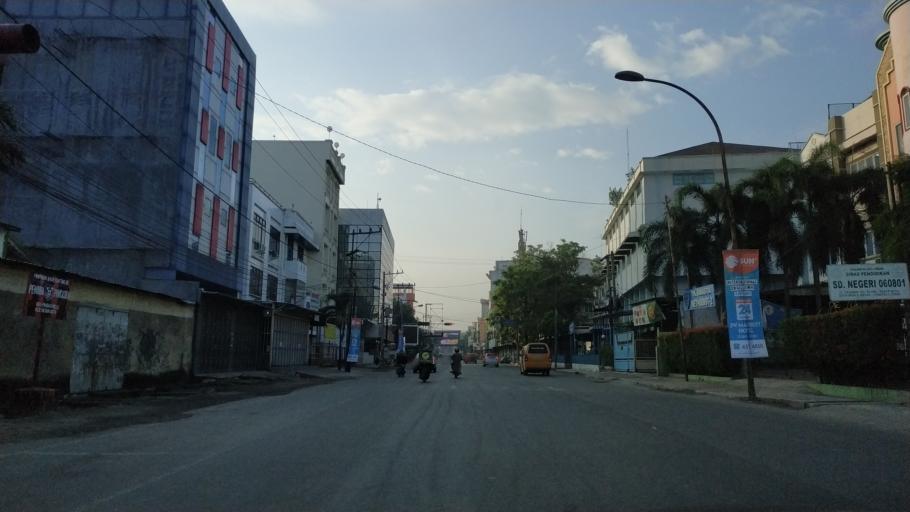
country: ID
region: North Sumatra
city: Medan
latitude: 3.5899
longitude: 98.6900
